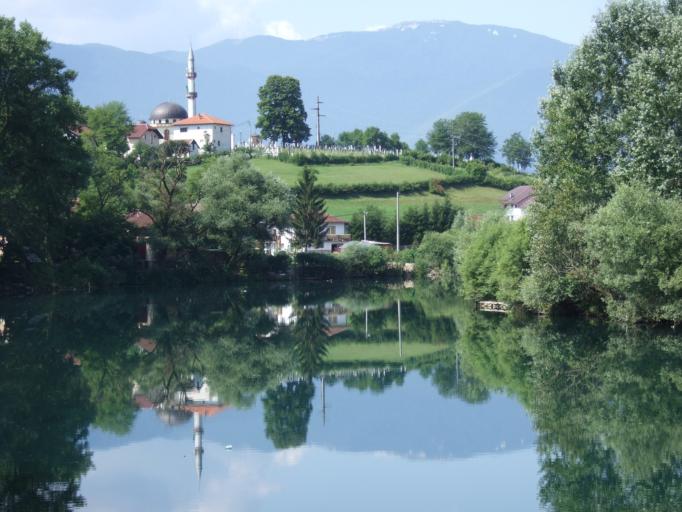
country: BA
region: Federation of Bosnia and Herzegovina
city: Bihac
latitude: 44.8575
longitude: 15.8834
